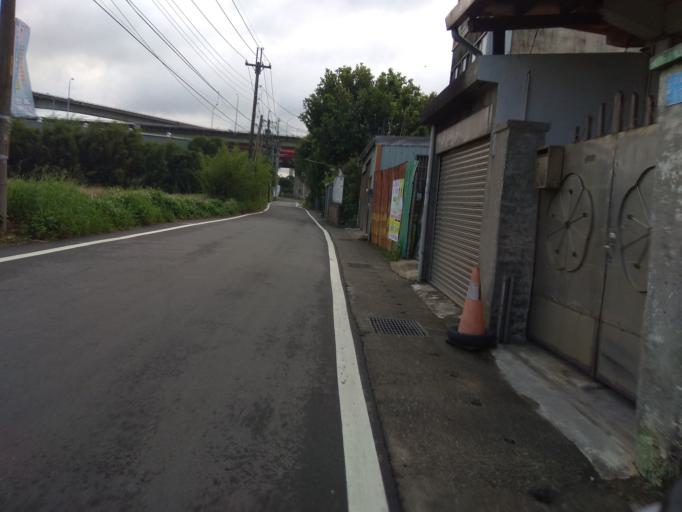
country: TW
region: Taiwan
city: Daxi
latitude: 24.9387
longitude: 121.1890
